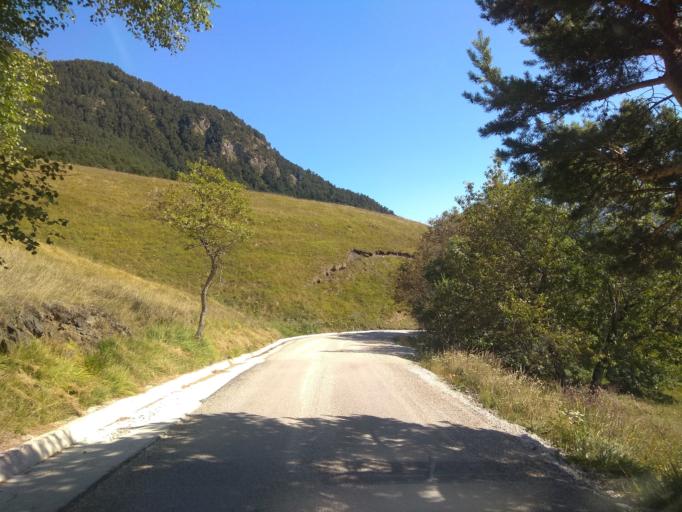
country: ES
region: Catalonia
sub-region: Provincia de Lleida
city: Les
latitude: 42.7622
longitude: 0.7093
